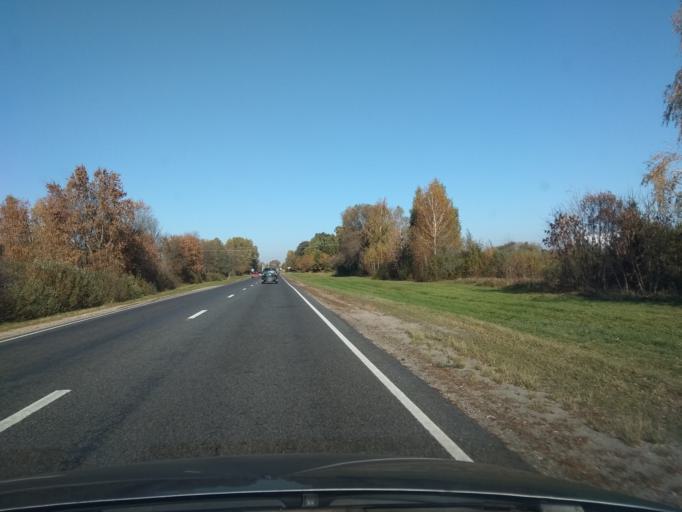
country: BY
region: Brest
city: Kobryn
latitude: 52.1522
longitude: 24.3097
